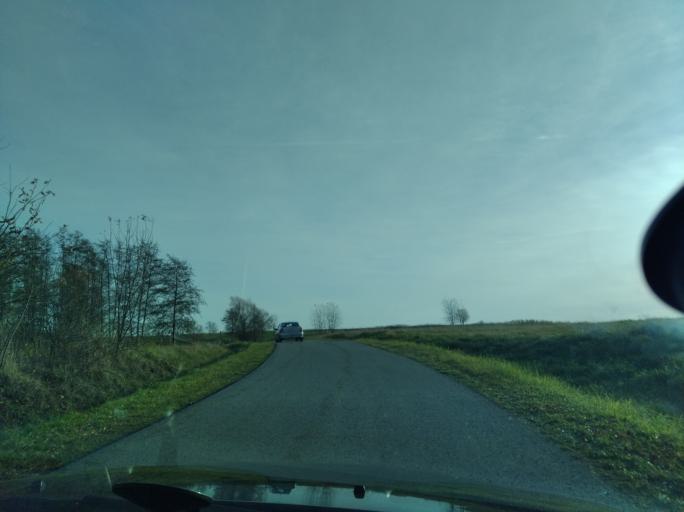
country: PL
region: Subcarpathian Voivodeship
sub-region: Powiat rzeszowski
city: Lubenia
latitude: 49.9350
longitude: 21.9379
